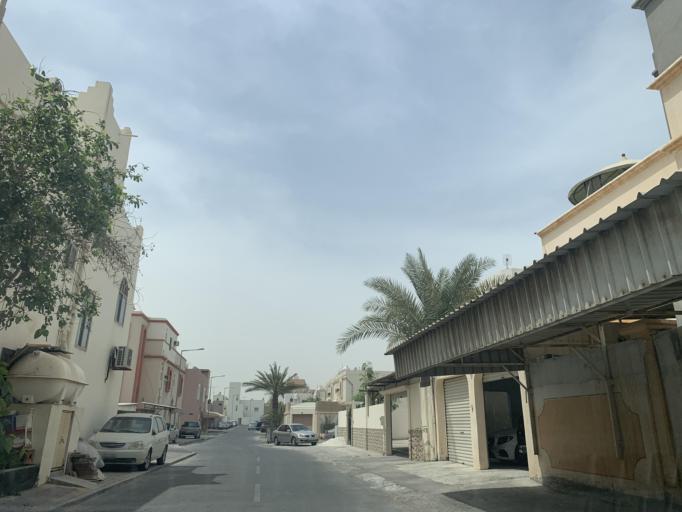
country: BH
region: Northern
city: Madinat `Isa
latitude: 26.1720
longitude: 50.5546
